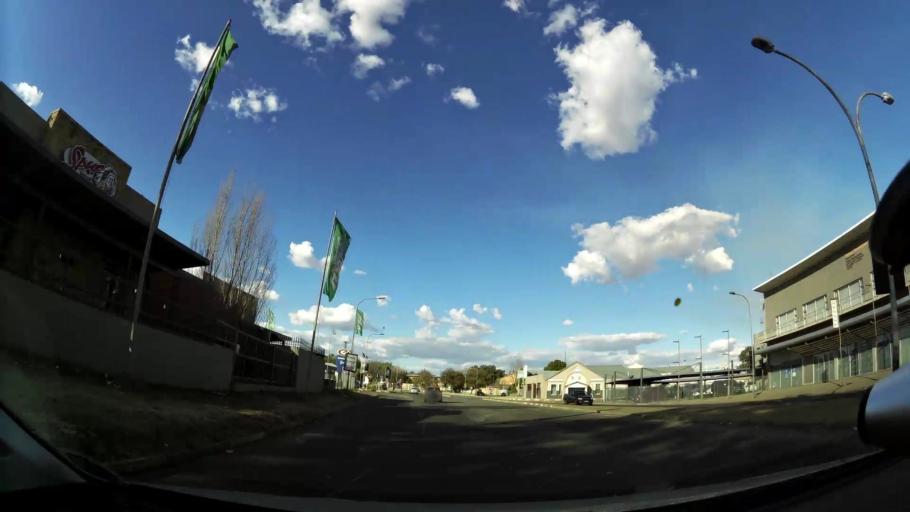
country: ZA
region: North-West
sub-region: Dr Kenneth Kaunda District Municipality
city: Klerksdorp
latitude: -26.8768
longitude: 26.6651
